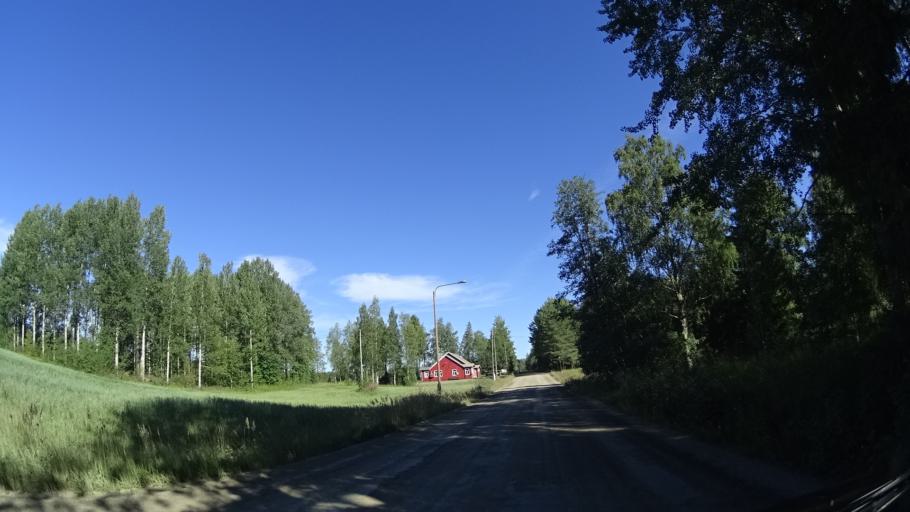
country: FI
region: Central Finland
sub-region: Jyvaeskylae
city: Petaejaevesi
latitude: 62.3548
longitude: 25.3242
